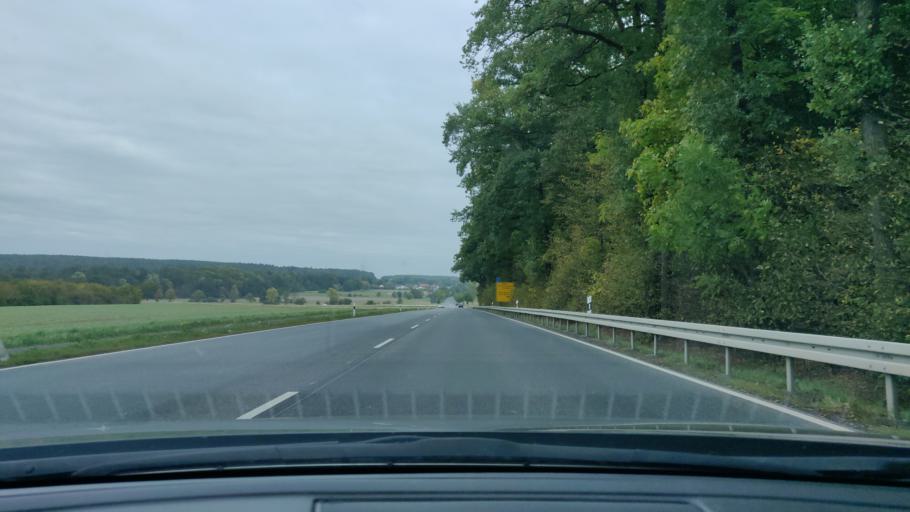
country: DE
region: Hesse
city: Schwalmstadt
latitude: 50.9321
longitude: 9.2640
